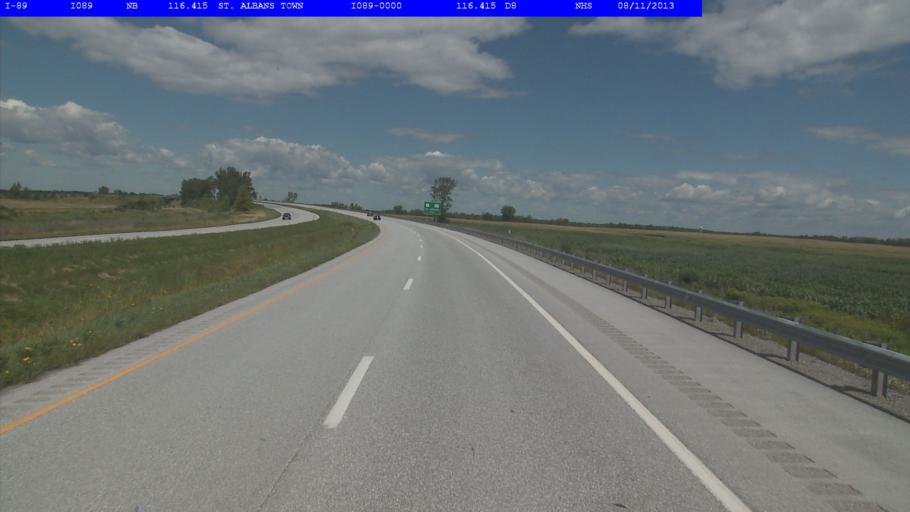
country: US
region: Vermont
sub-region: Franklin County
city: Saint Albans
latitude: 44.8329
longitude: -73.0613
